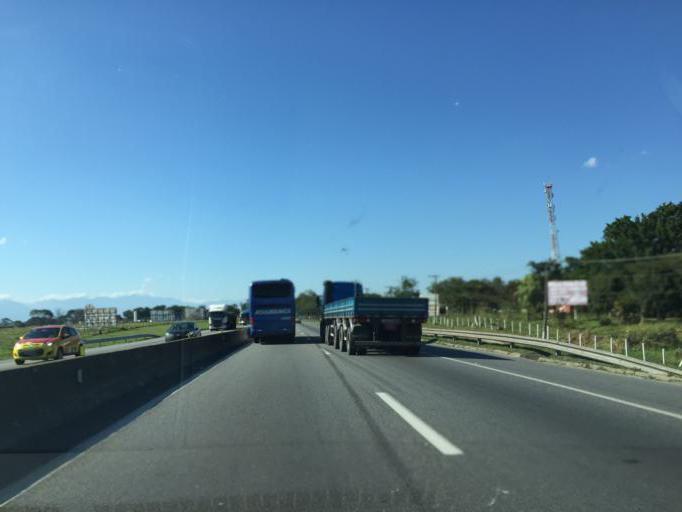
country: BR
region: Sao Paulo
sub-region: Lorena
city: Lorena
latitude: -22.7754
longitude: -45.1393
